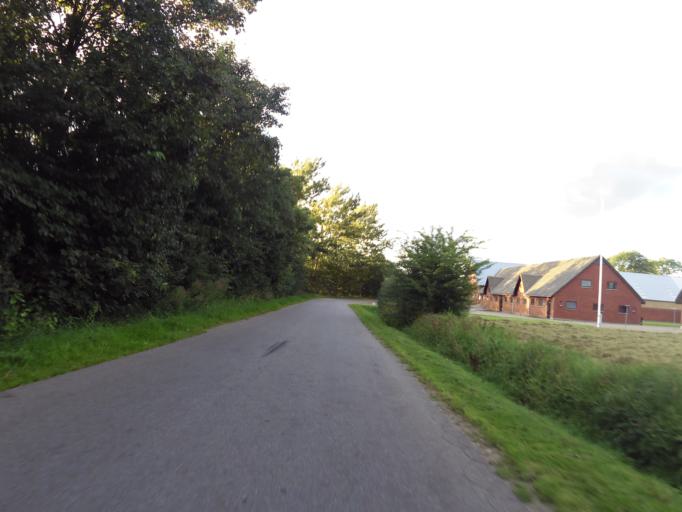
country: DK
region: South Denmark
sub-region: Tonder Kommune
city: Sherrebek
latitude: 55.2391
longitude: 8.8454
